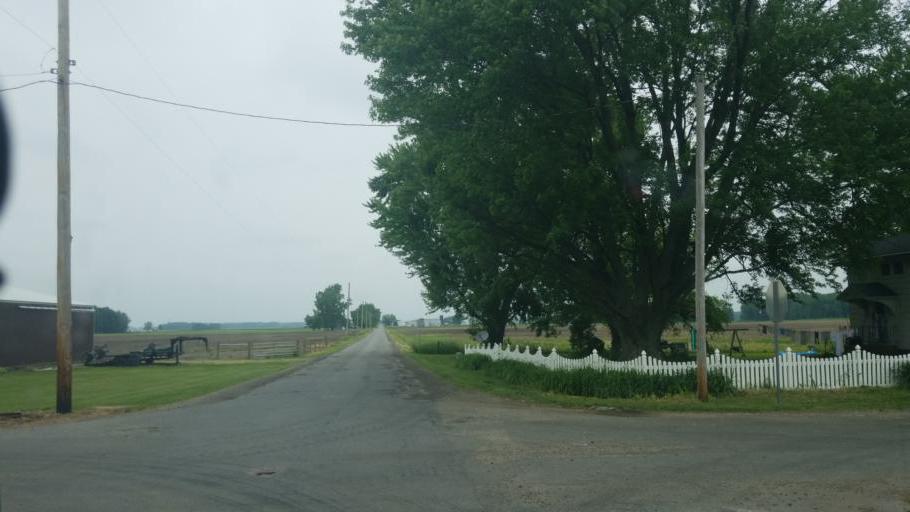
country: US
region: Indiana
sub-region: Marshall County
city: Bremen
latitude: 41.4934
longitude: -86.1179
